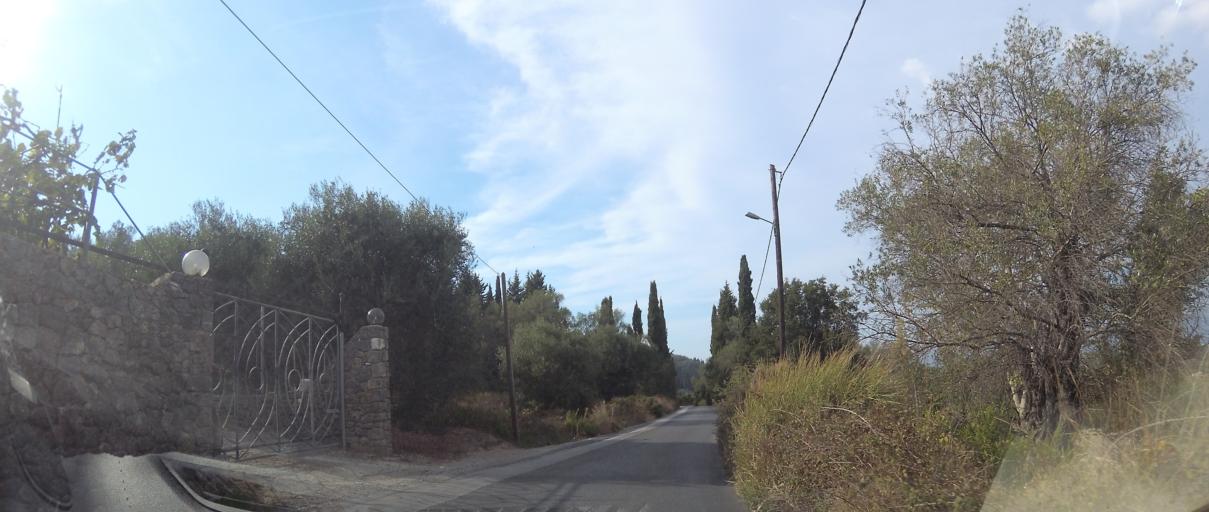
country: GR
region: Ionian Islands
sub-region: Nomos Kerkyras
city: Kynopiastes
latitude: 39.5571
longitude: 19.8570
